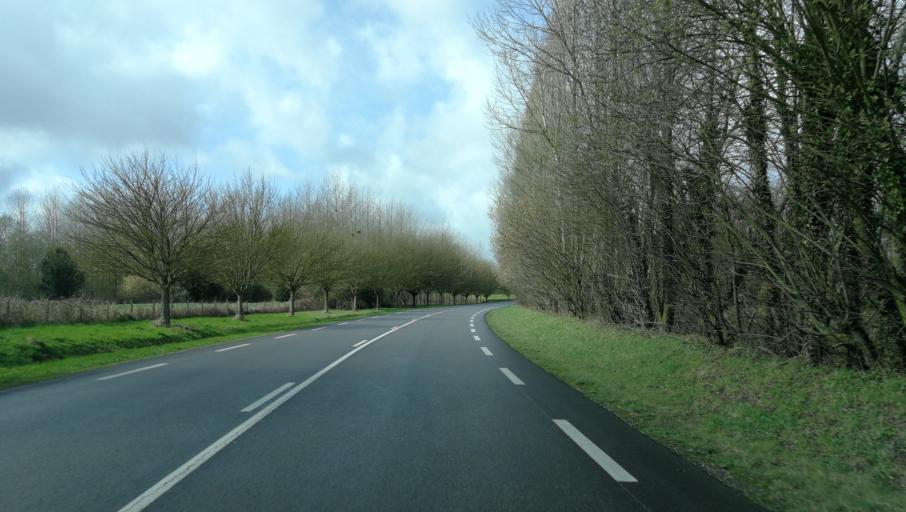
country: FR
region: Haute-Normandie
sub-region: Departement de l'Eure
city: Epaignes
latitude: 49.2741
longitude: 0.4425
